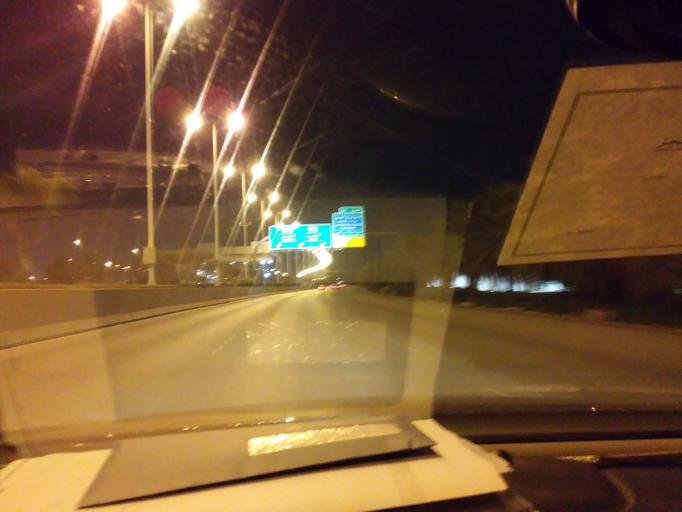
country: SA
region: Ar Riyad
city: Riyadh
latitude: 24.7221
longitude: 46.6951
